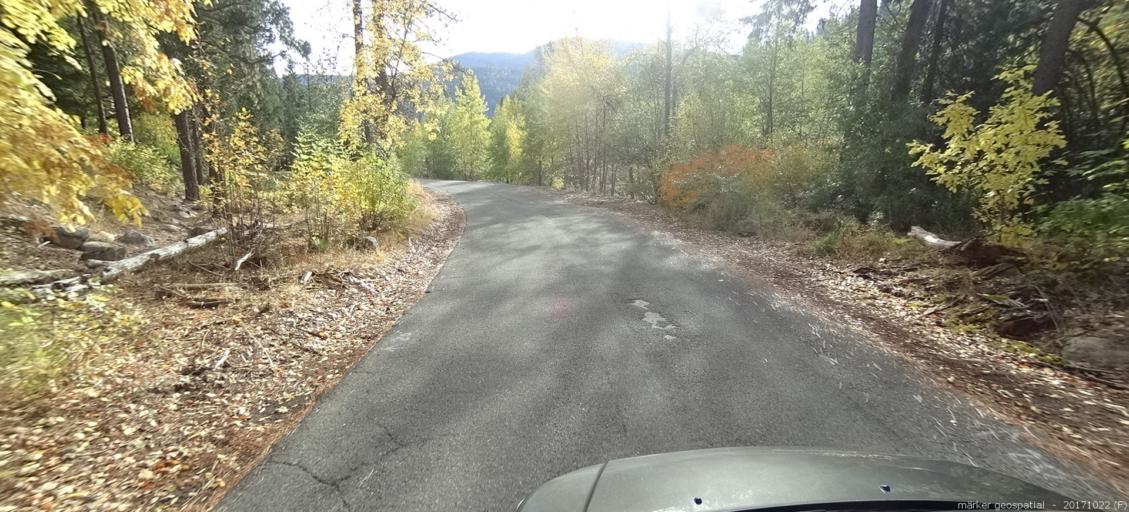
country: US
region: California
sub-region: Siskiyou County
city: Dunsmuir
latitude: 41.1475
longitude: -122.3257
